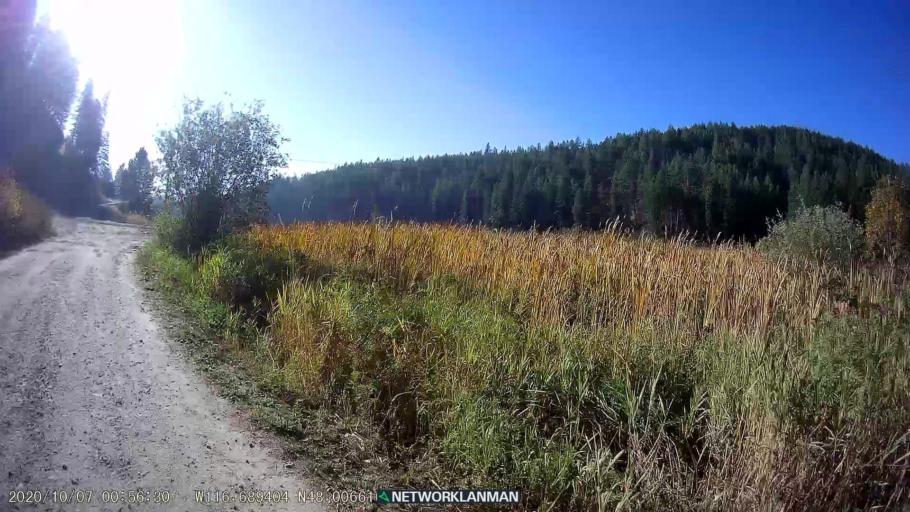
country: US
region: Idaho
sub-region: Kootenai County
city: Spirit Lake
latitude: 48.0050
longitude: -116.6872
